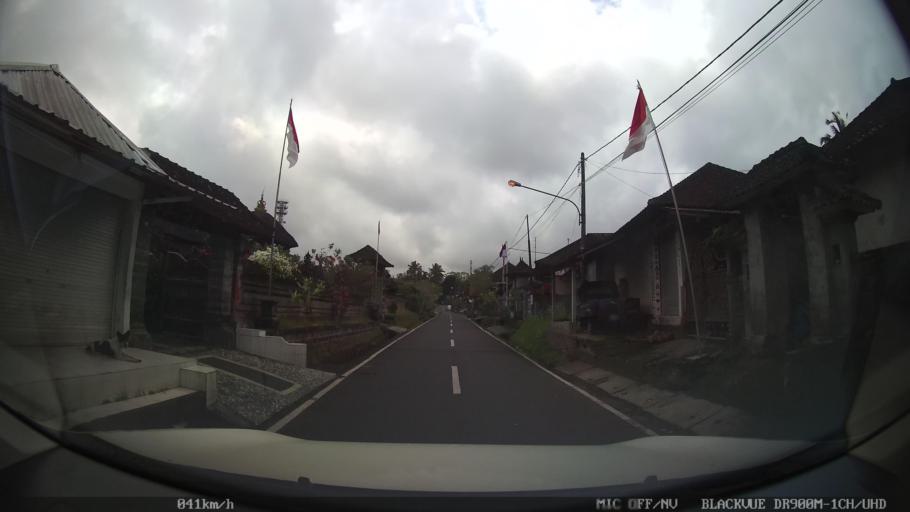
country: ID
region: Bali
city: Pemijian
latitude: -8.4449
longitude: 115.2267
